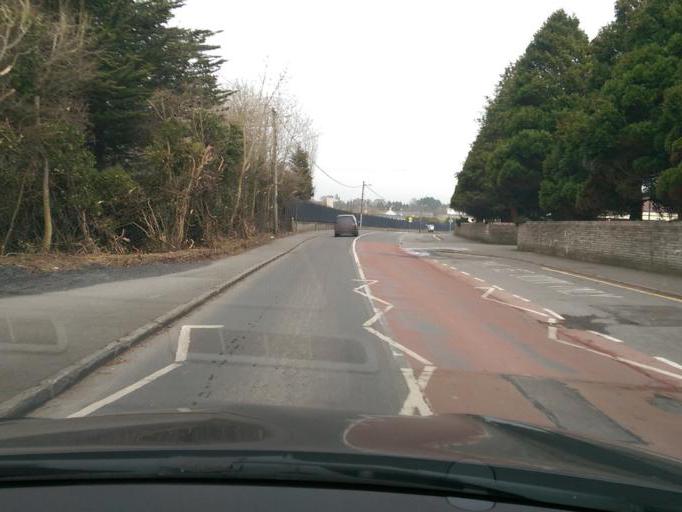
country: IE
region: Leinster
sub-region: An Iarmhi
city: Athlone
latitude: 53.4253
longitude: -7.9327
